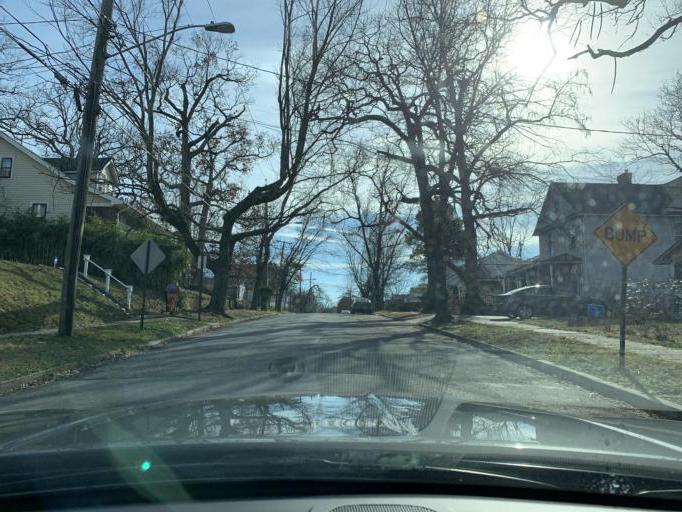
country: US
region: Maryland
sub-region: Prince George's County
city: Mount Rainier
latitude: 38.9403
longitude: -76.9659
